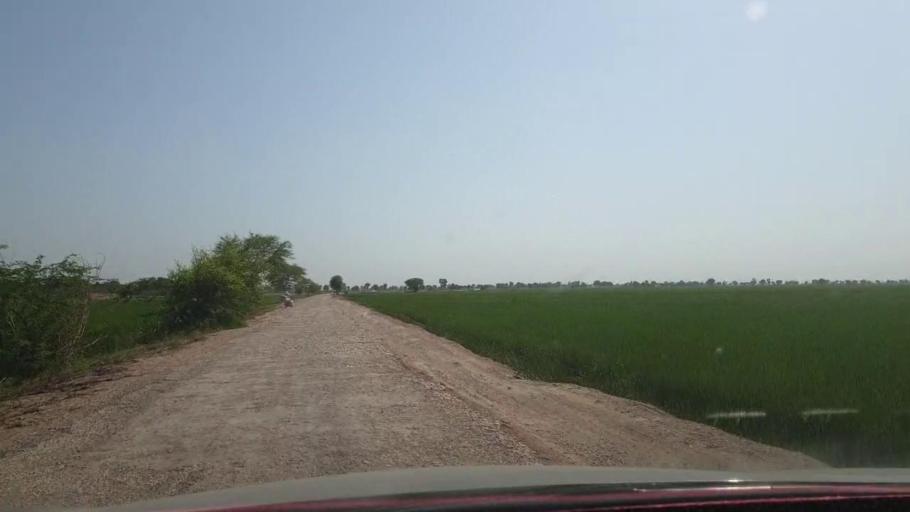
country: PK
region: Sindh
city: Nasirabad
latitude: 27.3608
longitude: 67.8508
